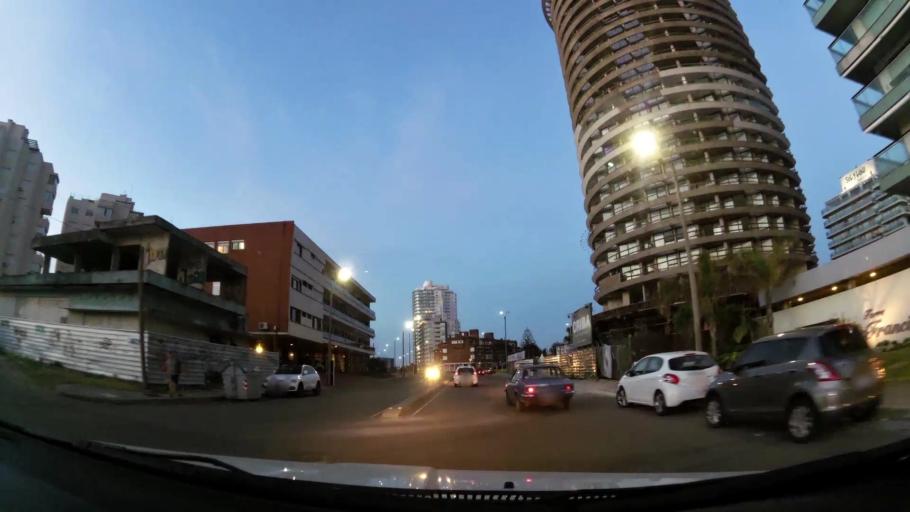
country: UY
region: Maldonado
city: Punta del Este
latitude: -34.9525
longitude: -54.9363
